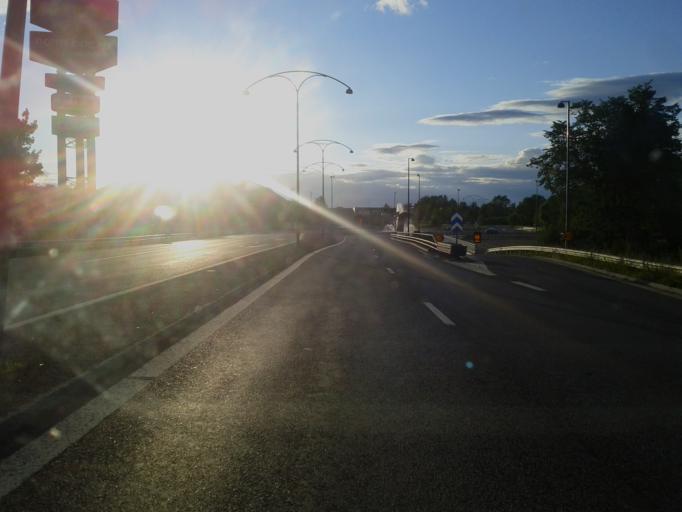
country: SE
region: Dalarna
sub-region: Borlange Kommun
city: Borlaenge
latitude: 60.4824
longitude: 15.4242
